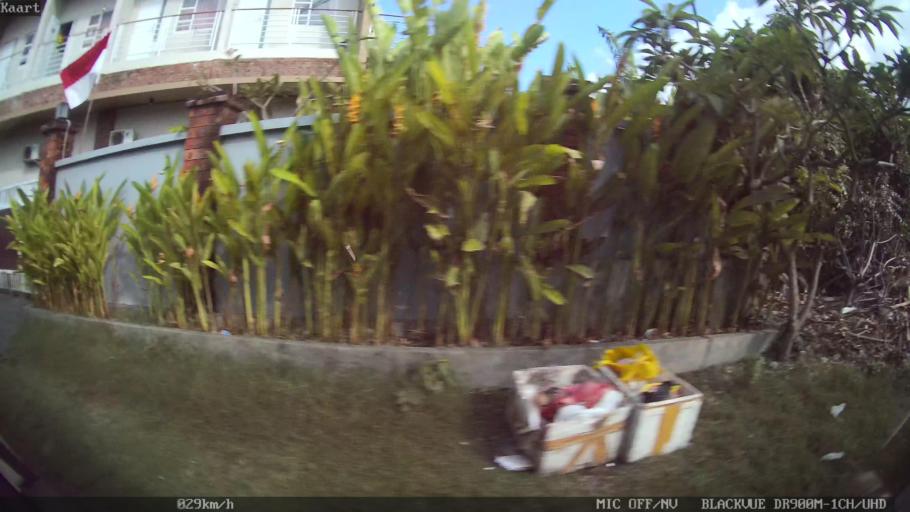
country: ID
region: Bali
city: Jabajero
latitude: -8.7174
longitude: 115.1887
